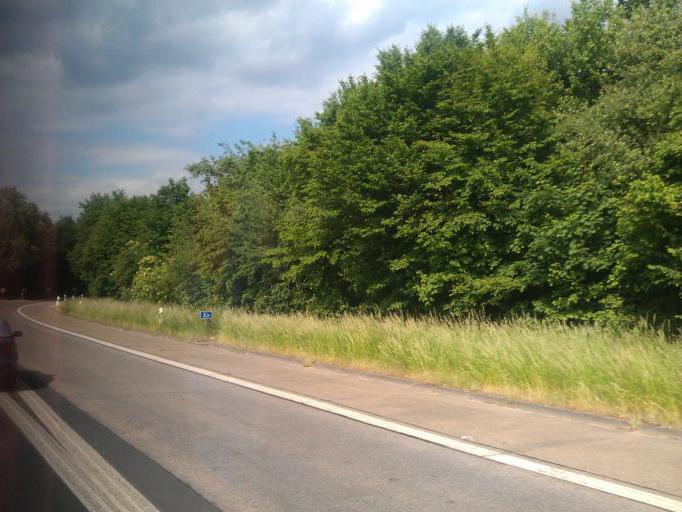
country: DE
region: North Rhine-Westphalia
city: Wesseling
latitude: 50.8657
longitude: 6.9698
